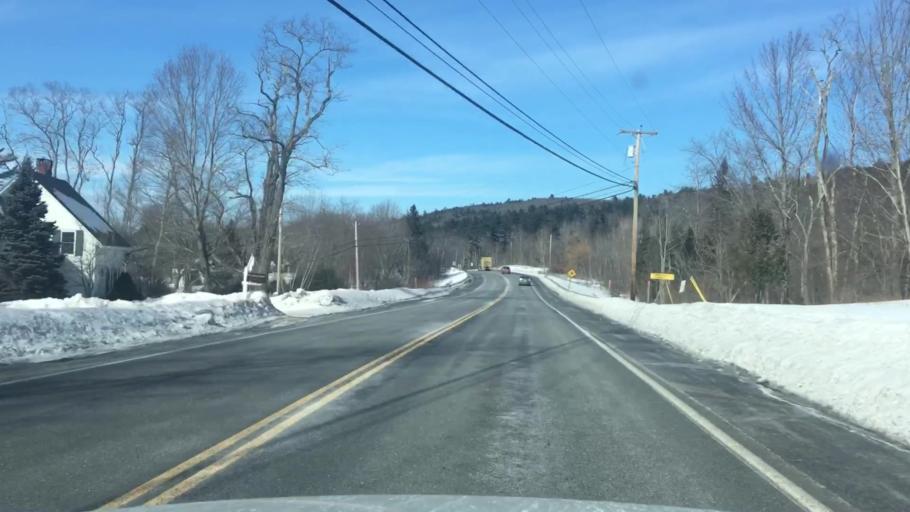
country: US
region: Maine
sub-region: Penobscot County
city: Orrington
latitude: 44.6878
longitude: -68.8108
